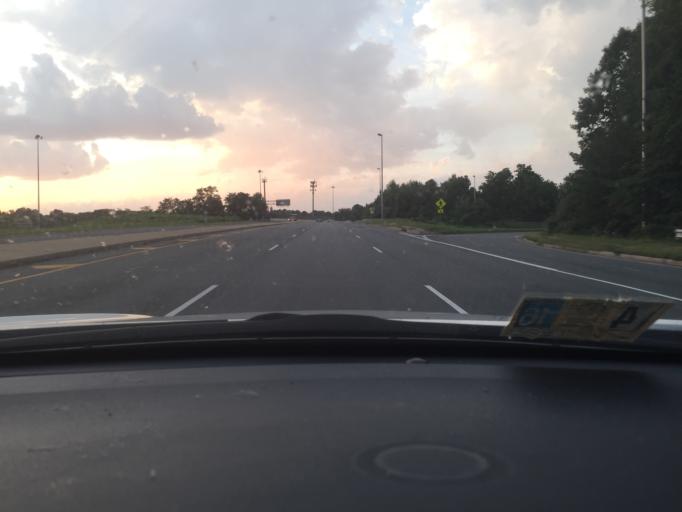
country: US
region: Virginia
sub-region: Fairfax County
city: Mantua
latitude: 38.8761
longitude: -77.2653
